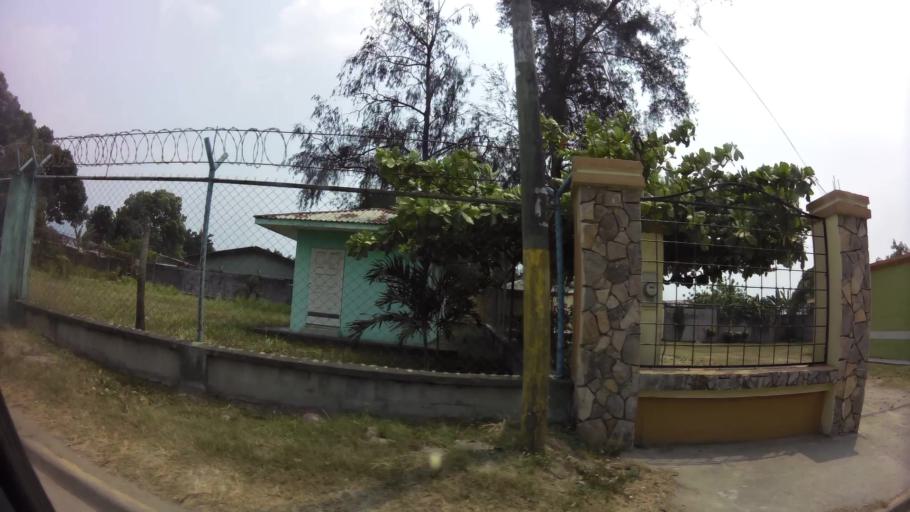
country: HN
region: Yoro
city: El Progreso
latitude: 15.3880
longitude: -87.8091
